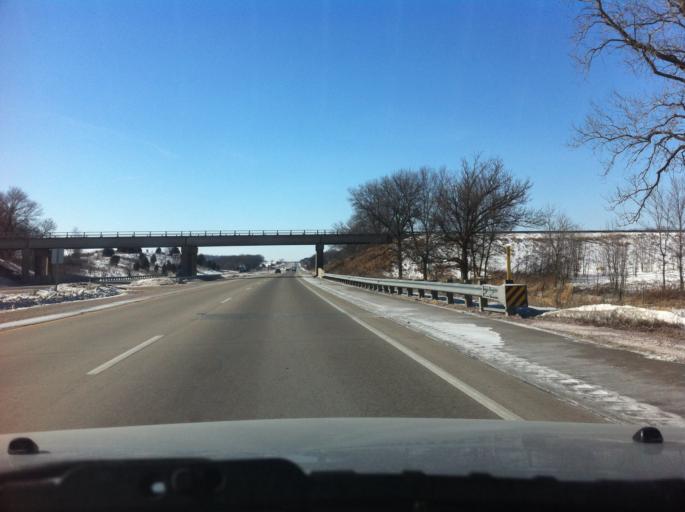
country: US
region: Wisconsin
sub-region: Sauk County
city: Baraboo
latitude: 43.5461
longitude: -89.6295
